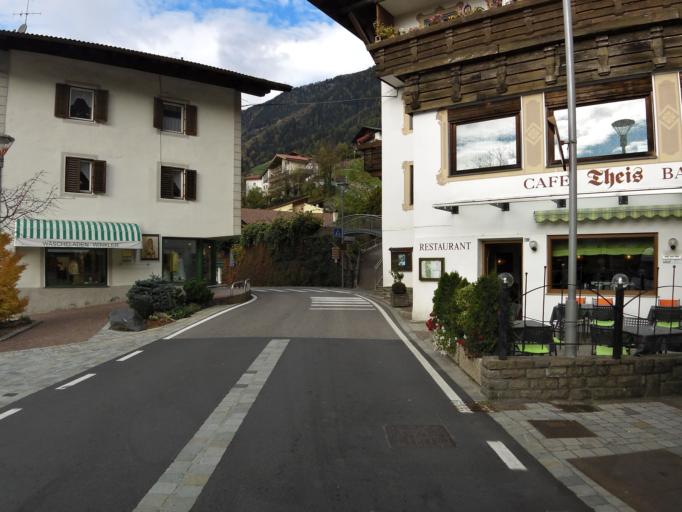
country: IT
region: Trentino-Alto Adige
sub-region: Bolzano
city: San Leonardo in Passiria
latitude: 46.8122
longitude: 11.2471
